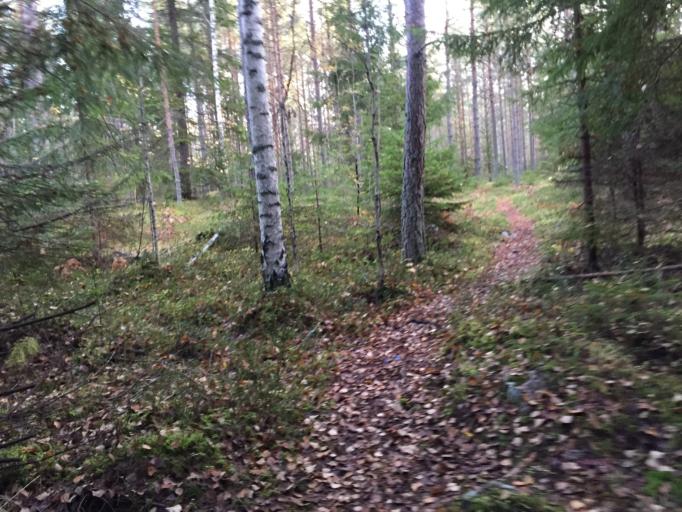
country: SE
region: Vaestmanland
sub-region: Hallstahammars Kommun
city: Hallstahammar
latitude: 59.6338
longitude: 16.2352
